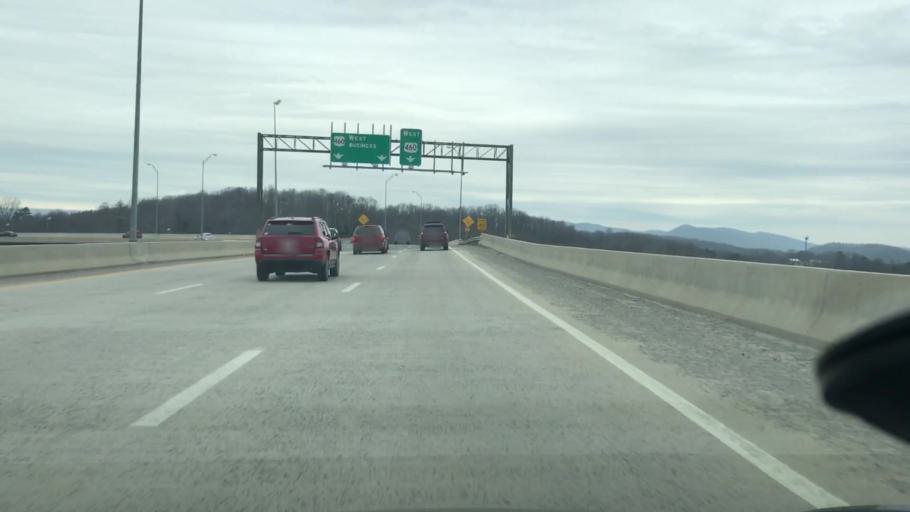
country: US
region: Virginia
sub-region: Montgomery County
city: Christiansburg
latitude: 37.1544
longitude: -80.4134
